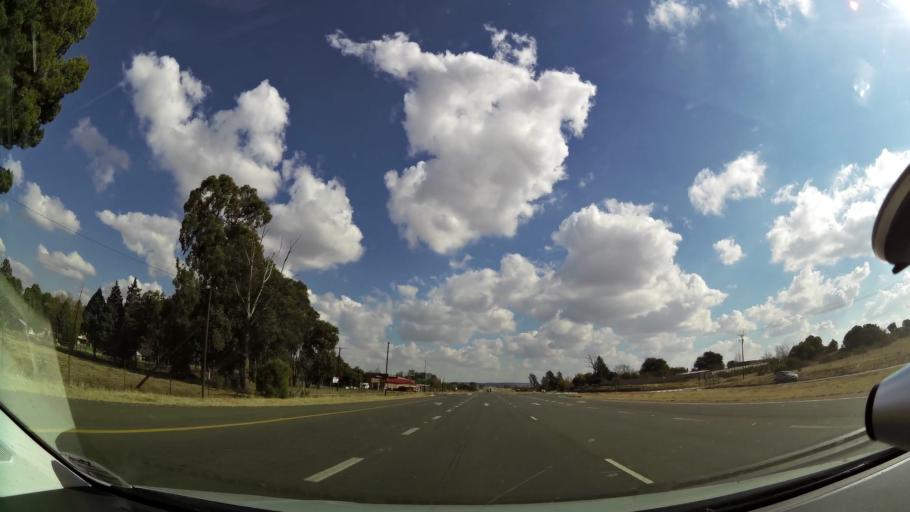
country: ZA
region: Orange Free State
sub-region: Mangaung Metropolitan Municipality
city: Bloemfontein
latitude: -29.1392
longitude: 26.1132
